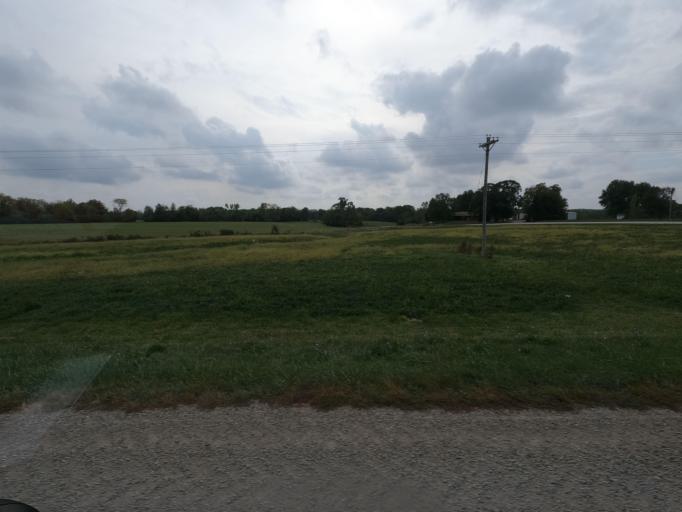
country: US
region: Iowa
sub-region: Wapello County
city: Ottumwa
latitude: 40.9508
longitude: -92.2350
